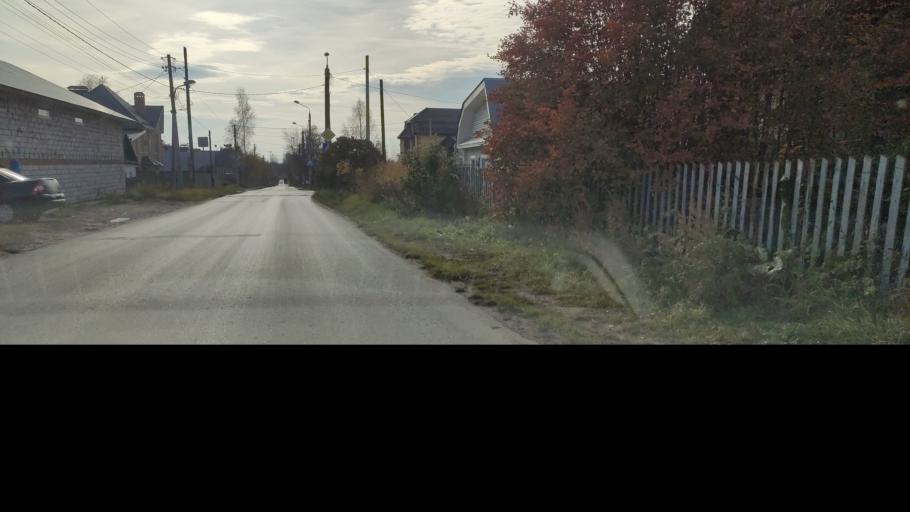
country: RU
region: Perm
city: Kondratovo
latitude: 58.0458
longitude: 56.1198
